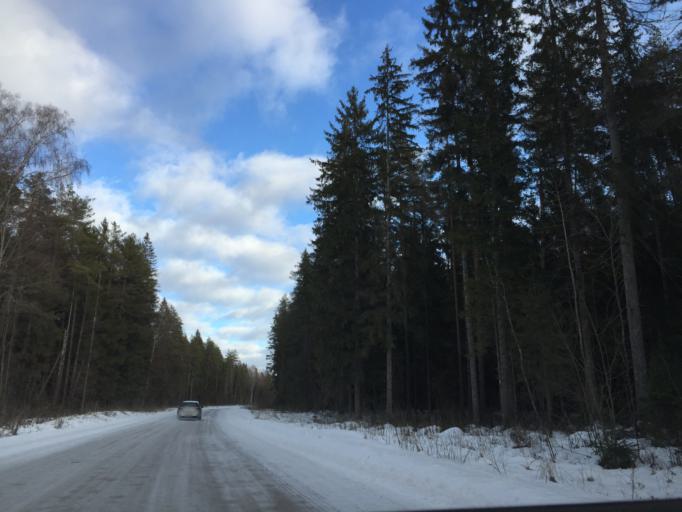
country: LV
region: Ogre
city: Jumprava
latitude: 56.5835
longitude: 24.9592
